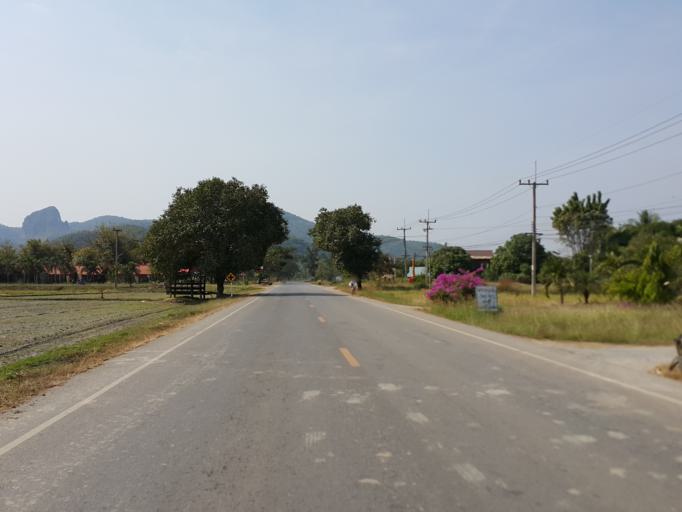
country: TH
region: Sukhothai
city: Thung Saliam
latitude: 17.3283
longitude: 99.5121
